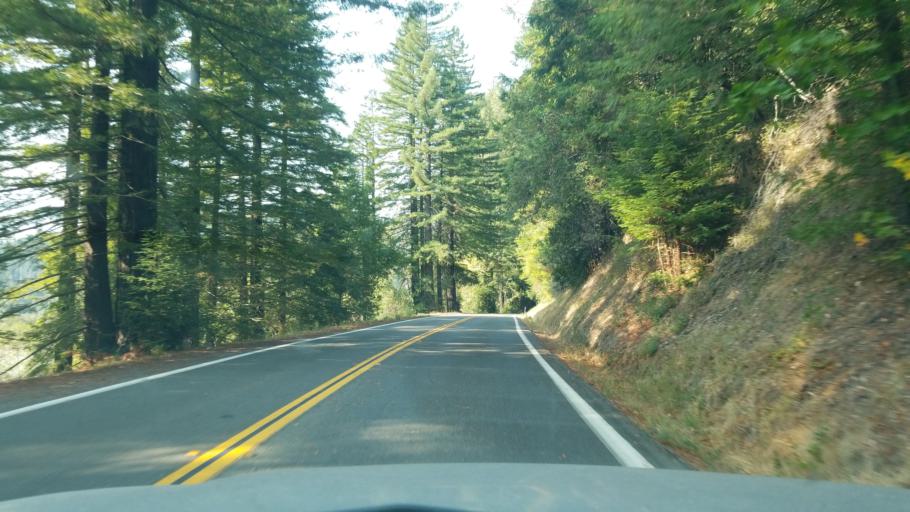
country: US
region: California
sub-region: Humboldt County
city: Redway
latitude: 40.2479
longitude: -123.8230
